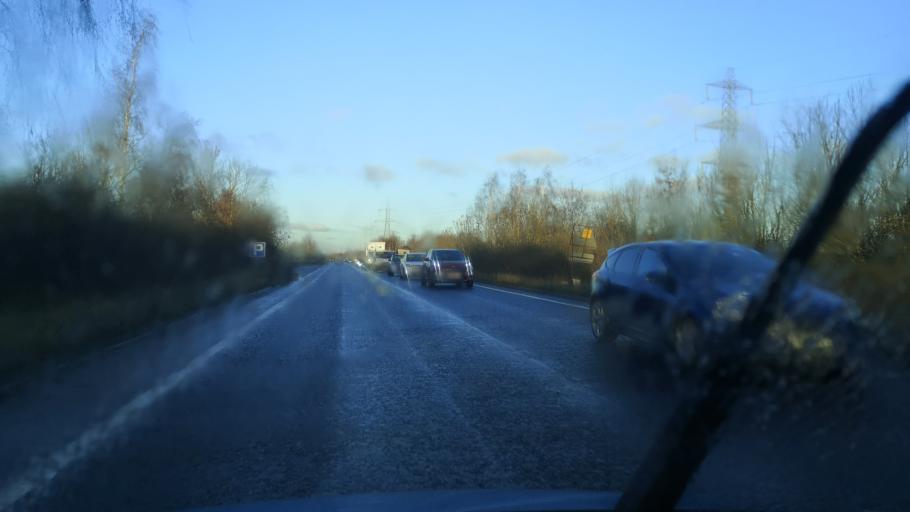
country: GB
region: England
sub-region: Barnsley
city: Darfield
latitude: 53.5193
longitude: -1.3652
